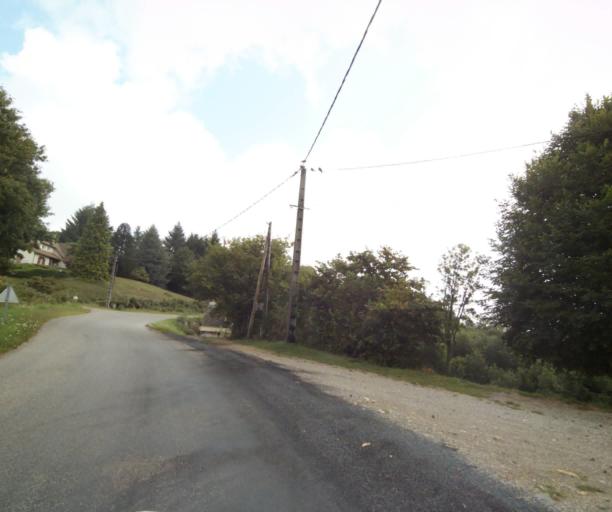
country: FR
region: Limousin
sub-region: Departement de la Correze
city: Sainte-Fortunade
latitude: 45.1926
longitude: 1.7832
